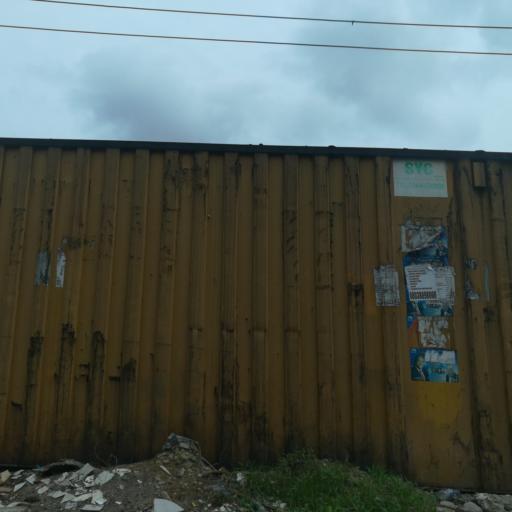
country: NG
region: Rivers
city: Port Harcourt
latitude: 4.8067
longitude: 7.0083
